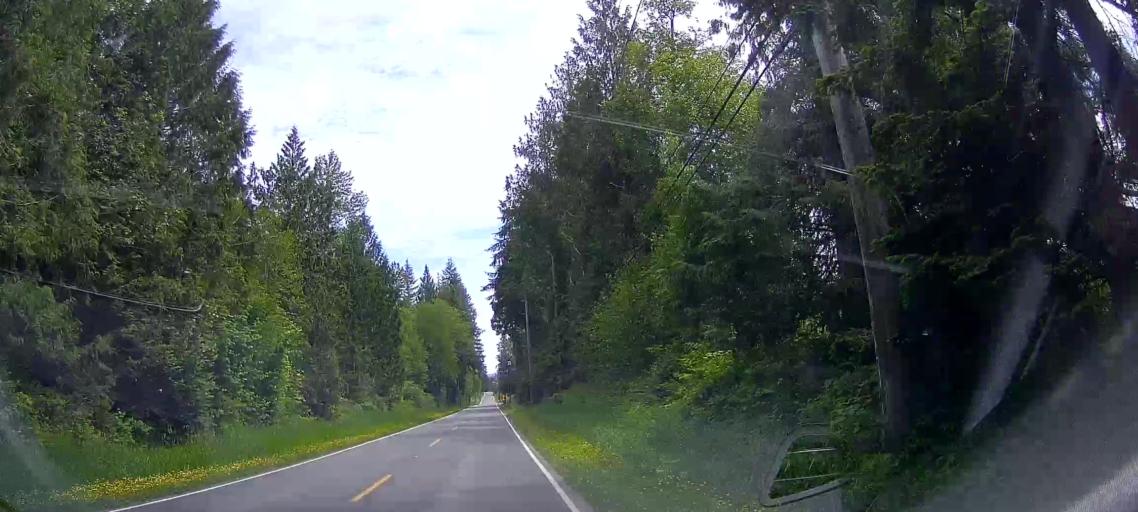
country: US
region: Washington
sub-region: Snohomish County
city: Bryant
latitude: 48.2388
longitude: -122.1685
